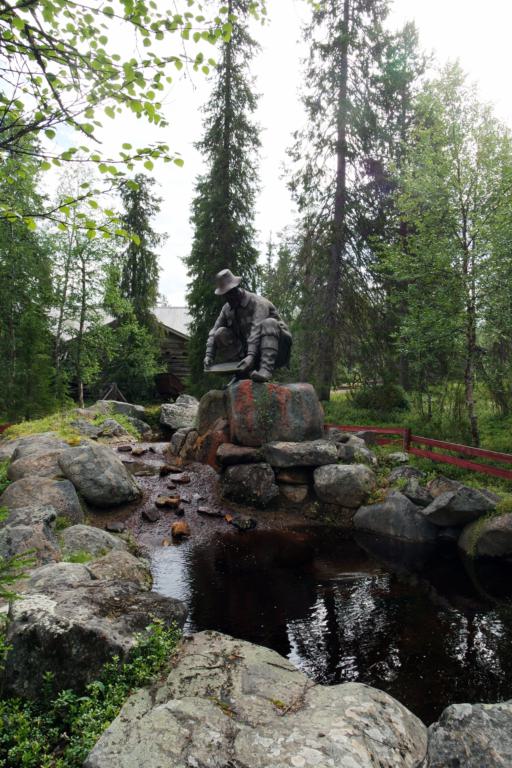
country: FI
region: Lapland
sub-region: Pohjois-Lappi
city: Ivalo
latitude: 68.1789
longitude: 27.1022
